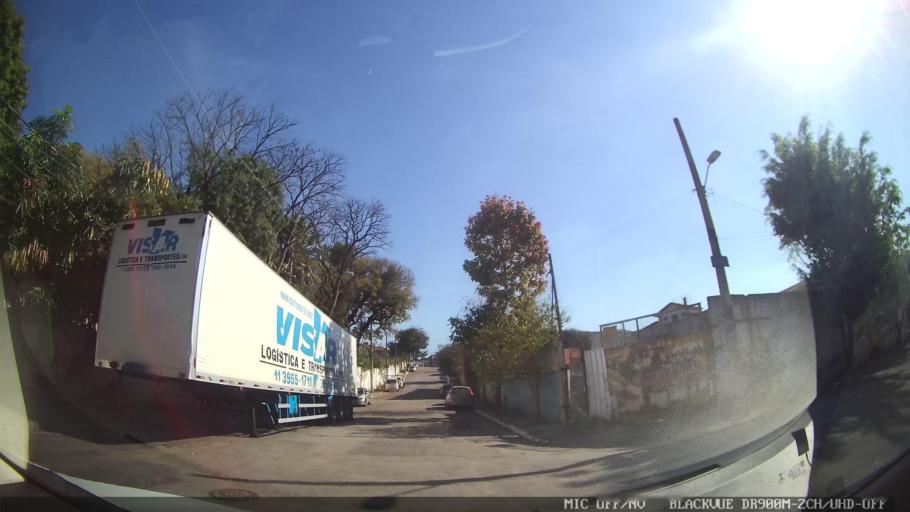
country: BR
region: Sao Paulo
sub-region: Sao Paulo
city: Sao Paulo
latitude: -23.4922
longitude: -46.6535
